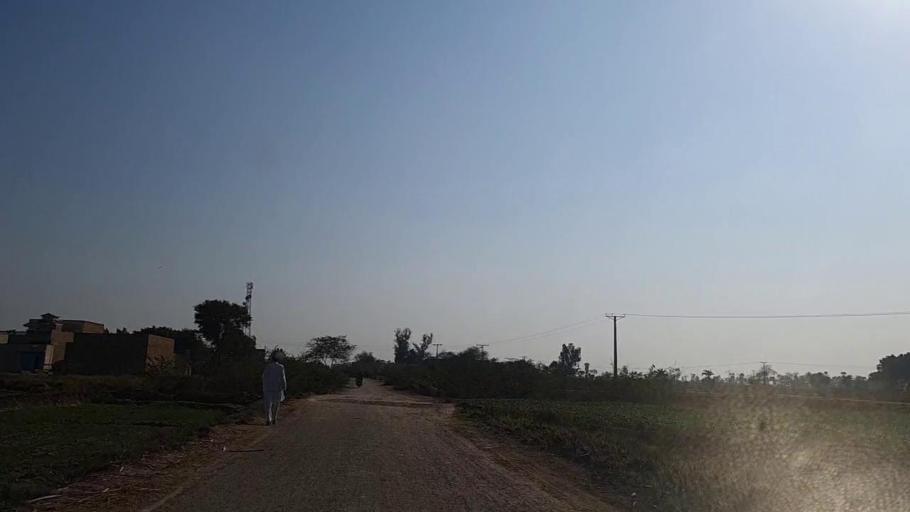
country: PK
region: Sindh
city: Daur
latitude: 26.4601
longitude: 68.3042
